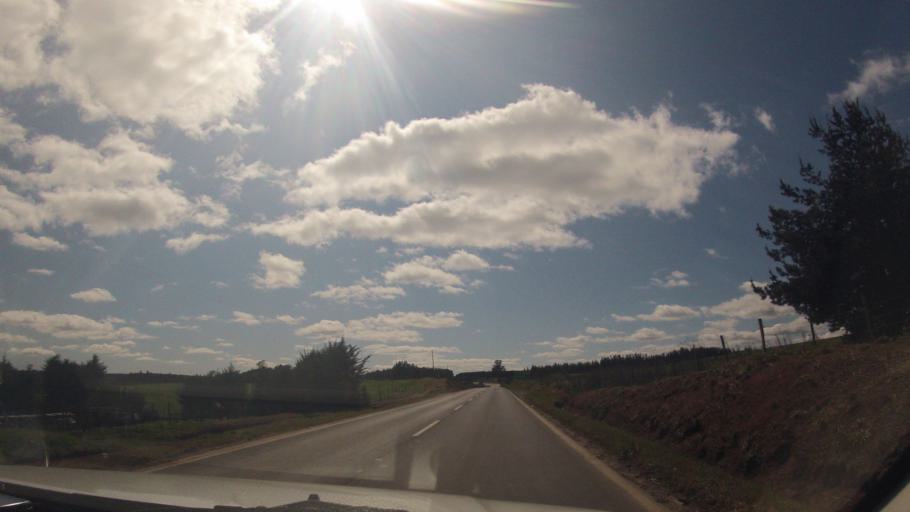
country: CL
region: Araucania
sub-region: Provincia de Malleco
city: Traiguen
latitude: -38.2234
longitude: -72.7085
